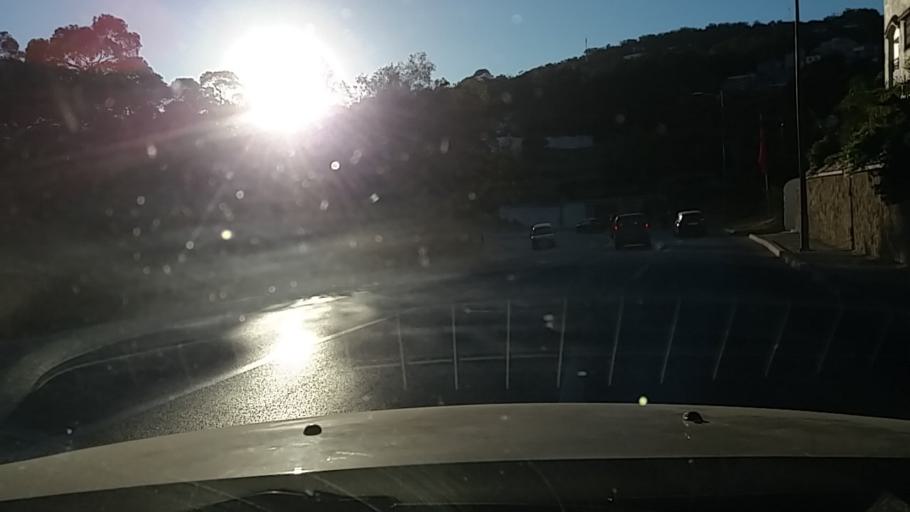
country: MA
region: Tanger-Tetouan
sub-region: Tanger-Assilah
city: Tangier
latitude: 35.7791
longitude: -5.8461
